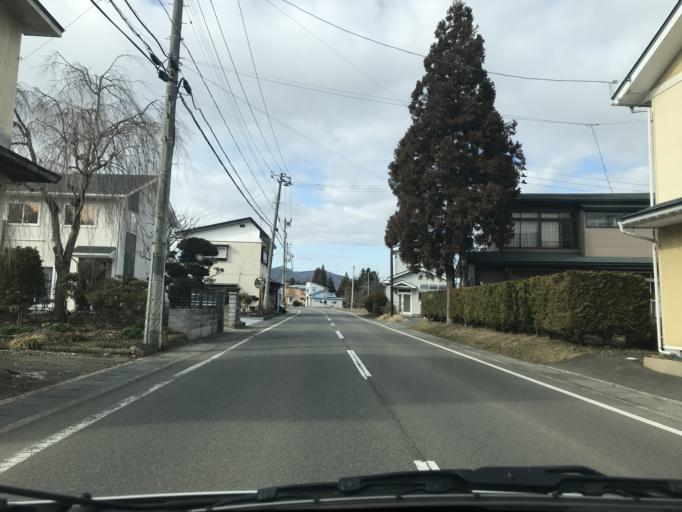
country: JP
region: Iwate
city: Hanamaki
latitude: 39.4227
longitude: 141.0853
